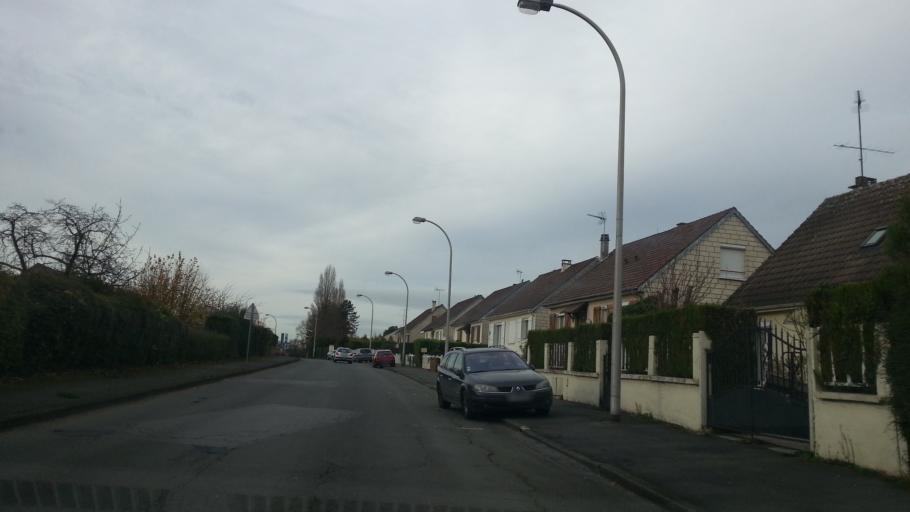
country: FR
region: Picardie
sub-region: Departement de l'Oise
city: Montataire
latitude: 49.2590
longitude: 2.4399
